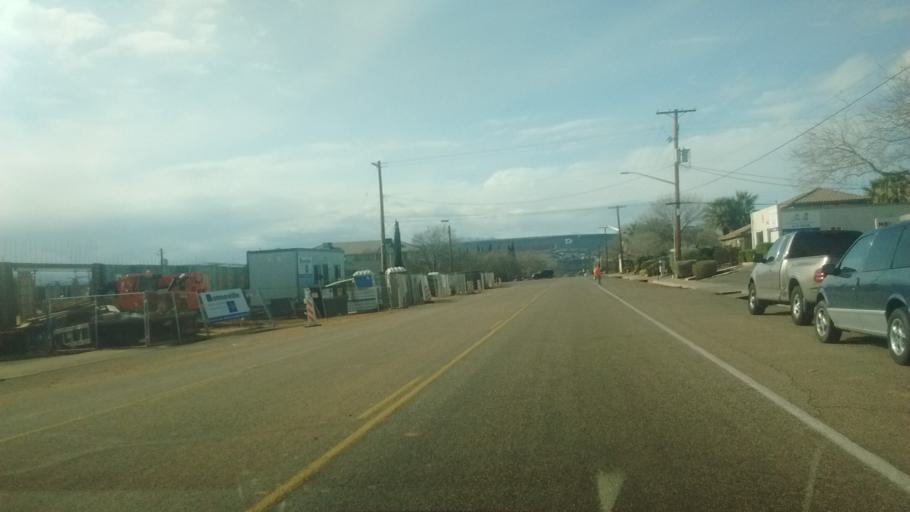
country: US
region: Utah
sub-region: Washington County
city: Saint George
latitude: 37.1082
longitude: -113.5646
